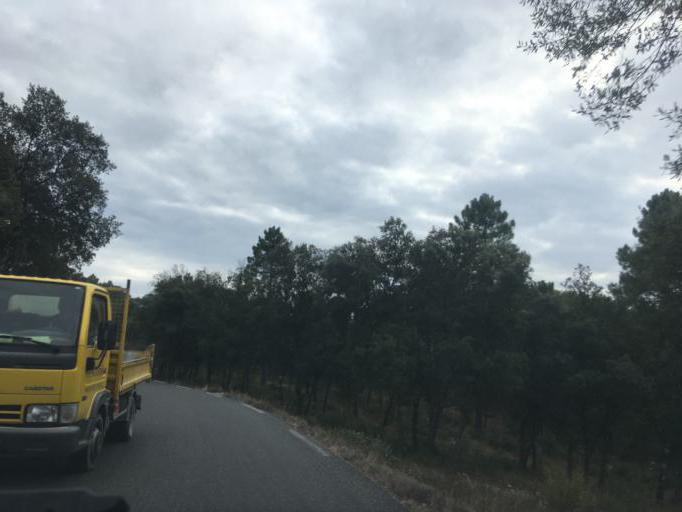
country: FR
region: Provence-Alpes-Cote d'Azur
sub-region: Departement du Var
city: Villecroze
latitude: 43.5495
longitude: 6.3265
